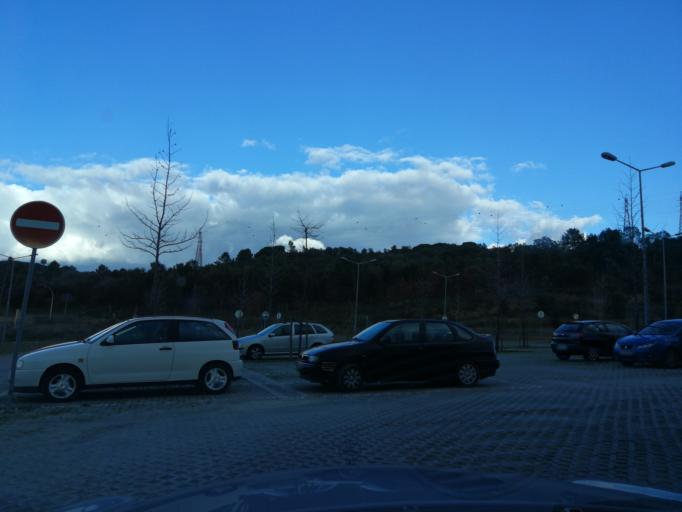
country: PT
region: Braga
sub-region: Braga
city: Adaufe
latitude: 41.5695
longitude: -8.3998
